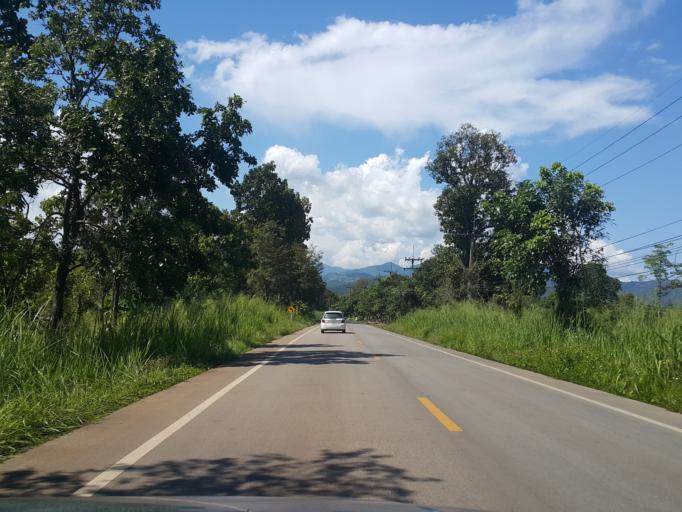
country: TH
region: Chiang Mai
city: Mae Taeng
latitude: 19.1612
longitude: 98.9399
